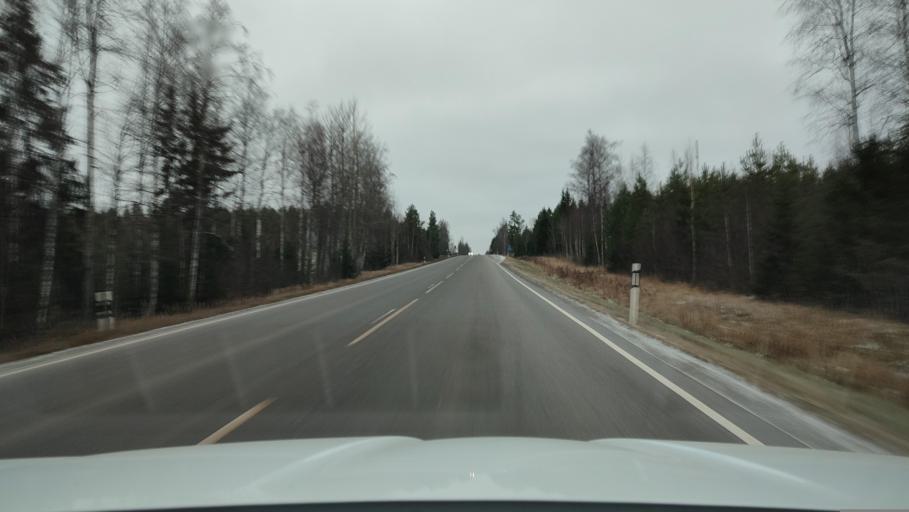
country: FI
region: Ostrobothnia
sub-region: Sydosterbotten
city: Naerpes
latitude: 62.5021
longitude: 21.4493
